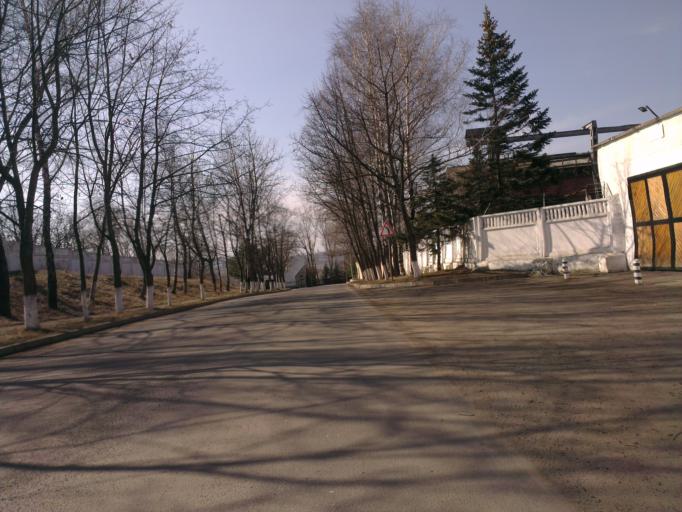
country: MD
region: Chisinau
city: Cricova
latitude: 47.1371
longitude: 28.8566
